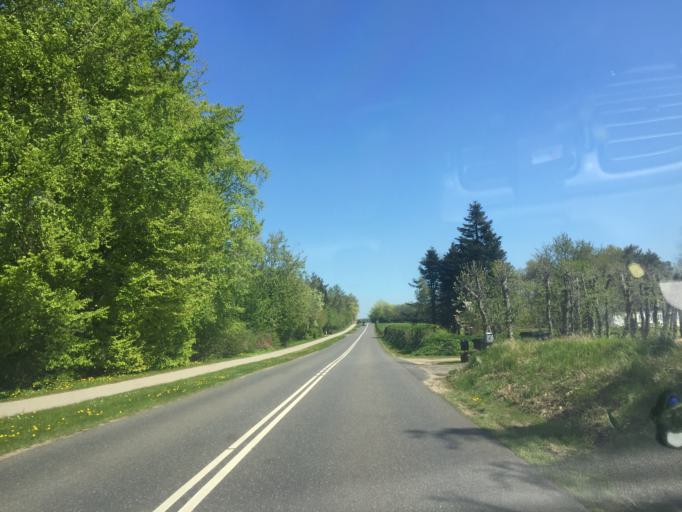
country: DK
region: Capital Region
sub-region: Egedal Kommune
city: Ganlose
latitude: 55.7834
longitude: 12.2481
